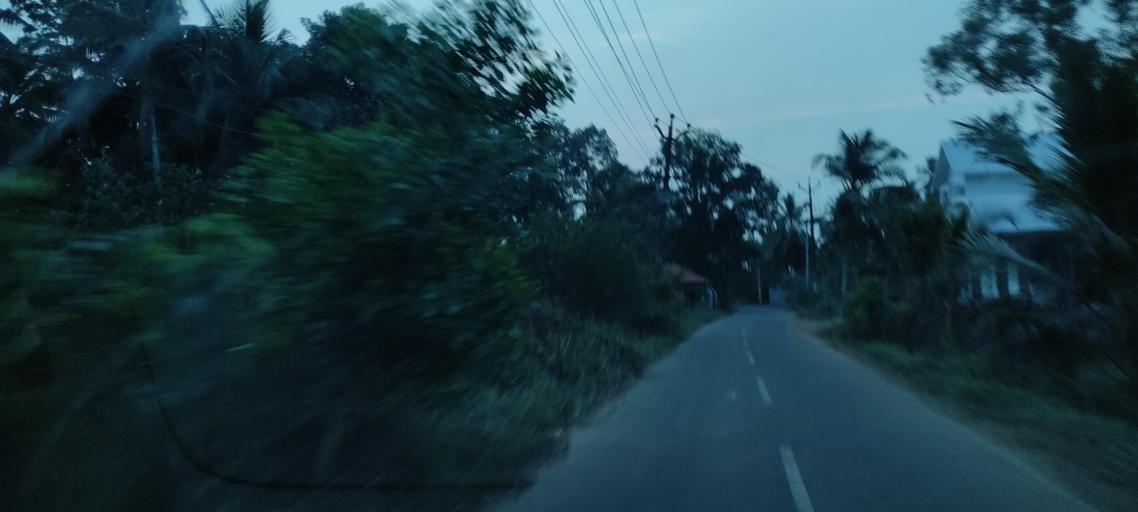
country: IN
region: Kerala
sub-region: Alappuzha
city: Mavelikara
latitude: 9.3306
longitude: 76.4959
